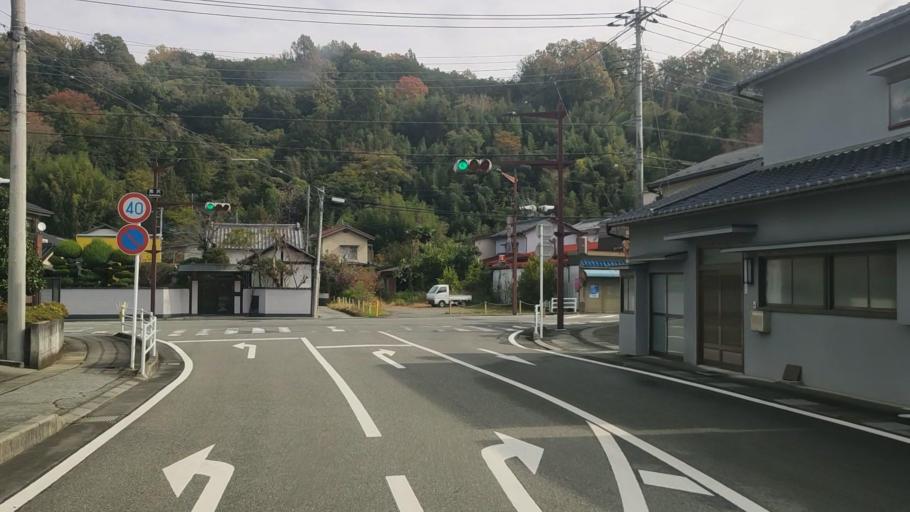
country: JP
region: Yamanashi
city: Ryuo
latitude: 35.5397
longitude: 138.4711
